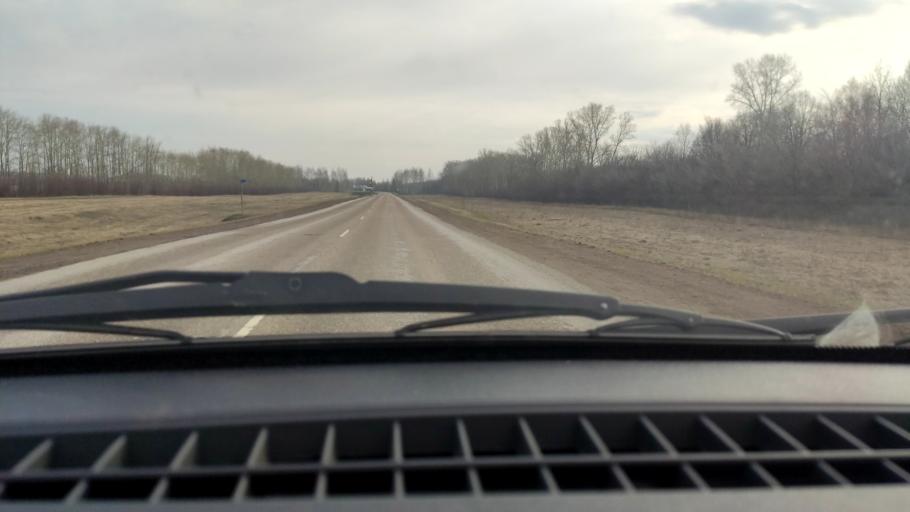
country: RU
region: Bashkortostan
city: Davlekanovo
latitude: 54.3578
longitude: 55.1895
